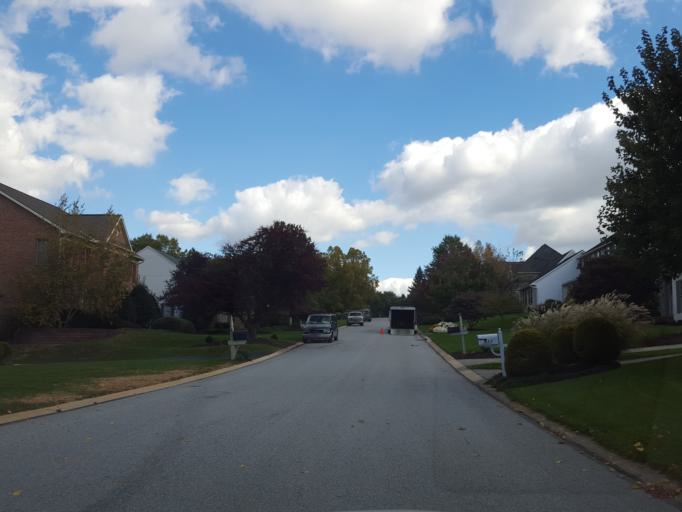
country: US
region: Pennsylvania
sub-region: York County
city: East York
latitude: 39.9541
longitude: -76.6675
